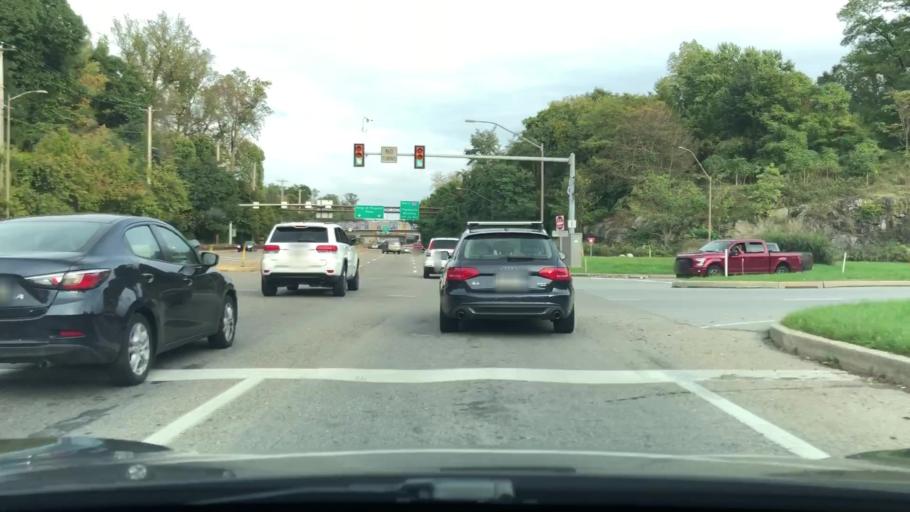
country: US
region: Pennsylvania
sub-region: Delaware County
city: Radnor
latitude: 40.0374
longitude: -75.3599
